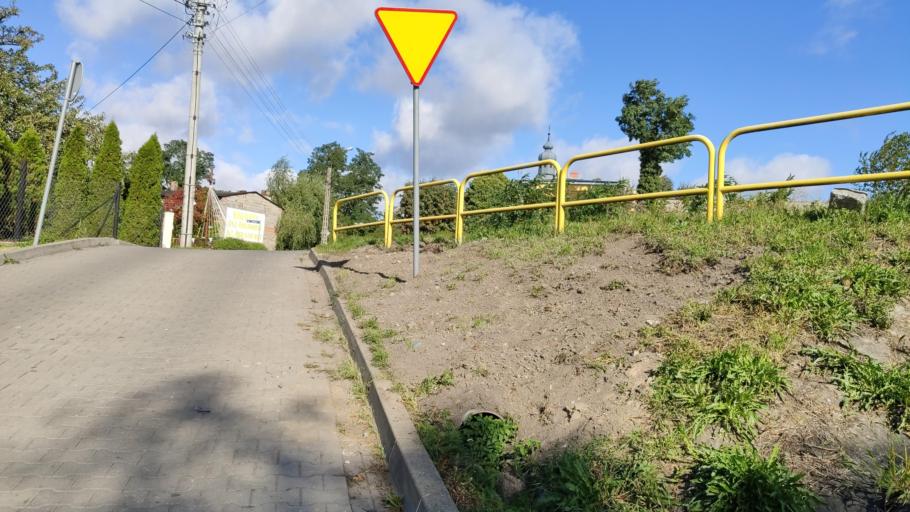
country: PL
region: Kujawsko-Pomorskie
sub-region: Powiat zninski
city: Znin
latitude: 52.8533
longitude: 17.7563
